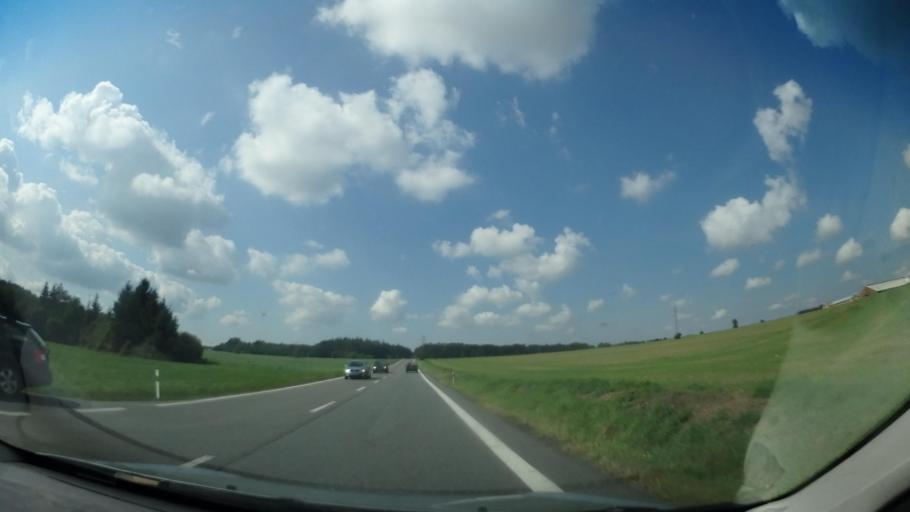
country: CZ
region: Central Bohemia
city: Kostelec nad Cernymi Lesy
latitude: 49.9820
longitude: 14.8841
